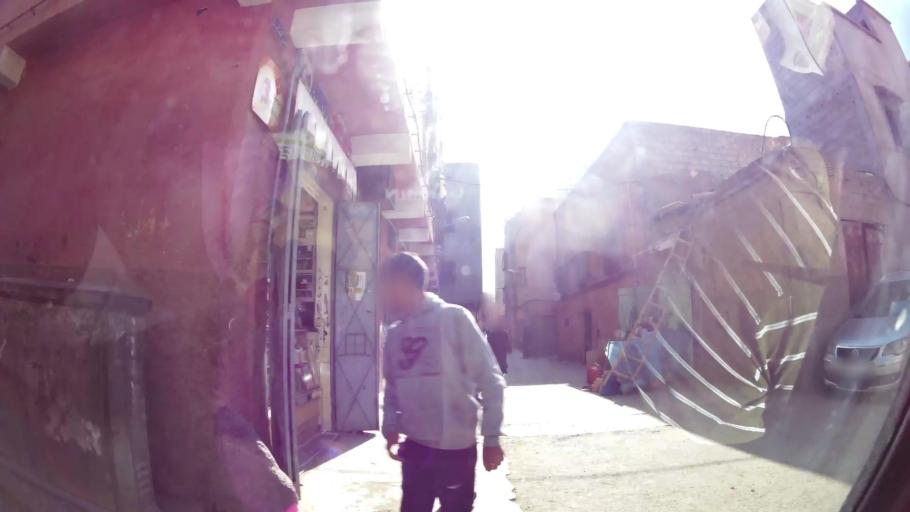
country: MA
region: Marrakech-Tensift-Al Haouz
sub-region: Marrakech
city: Marrakesh
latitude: 31.6146
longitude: -7.9662
